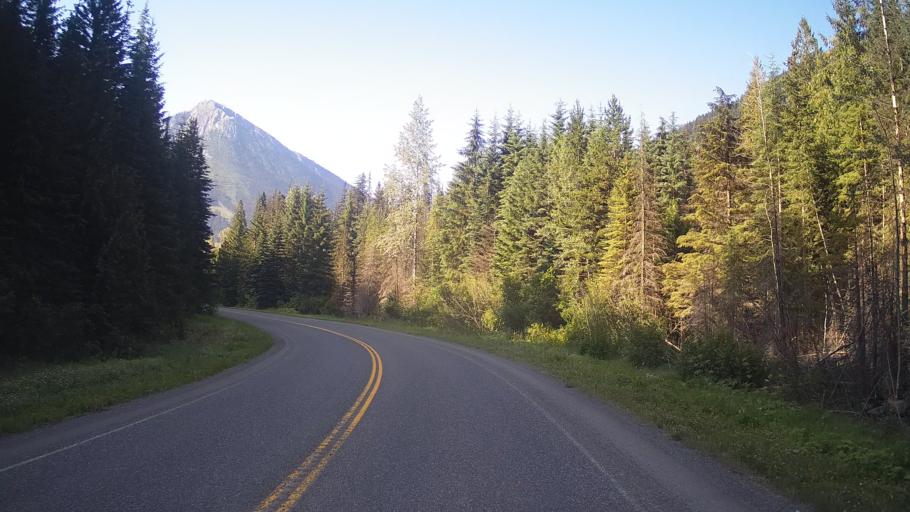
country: CA
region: British Columbia
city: Lillooet
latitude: 50.4496
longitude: -122.2521
